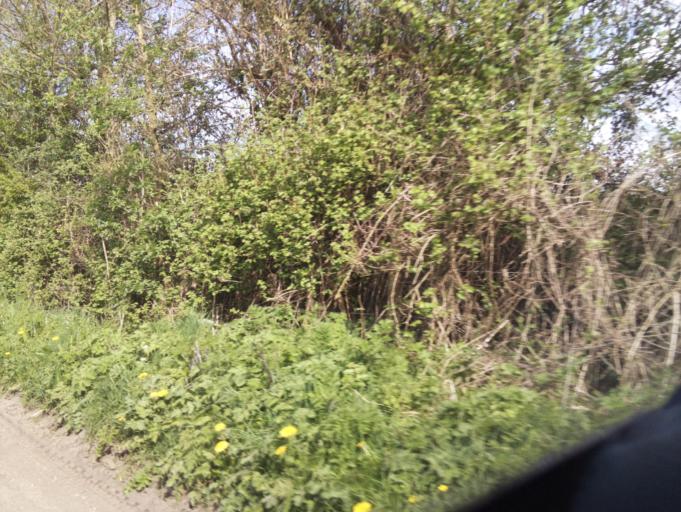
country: GB
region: England
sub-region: Hampshire
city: Abbotts Ann
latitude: 51.1256
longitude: -1.4940
